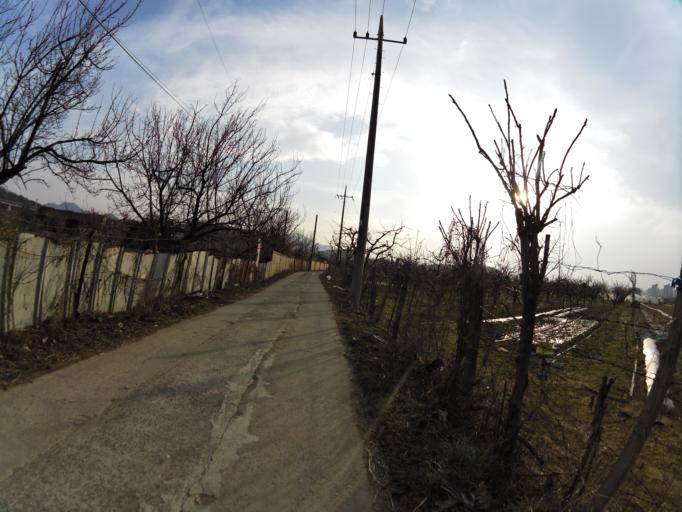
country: KR
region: Gyeongsangbuk-do
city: Gyeongsan-si
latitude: 35.8571
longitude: 128.7159
